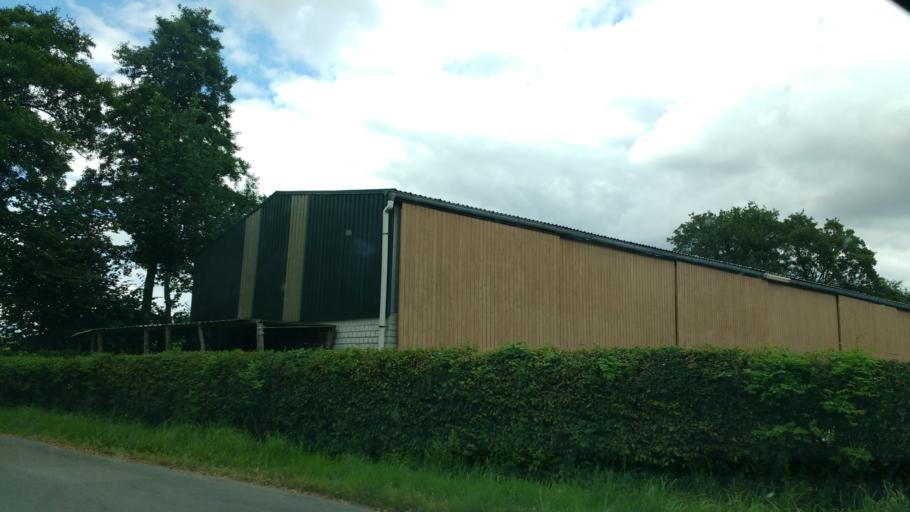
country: DE
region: North Rhine-Westphalia
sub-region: Regierungsbezirk Detmold
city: Horn-Bad Meinberg
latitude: 51.9108
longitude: 8.9277
